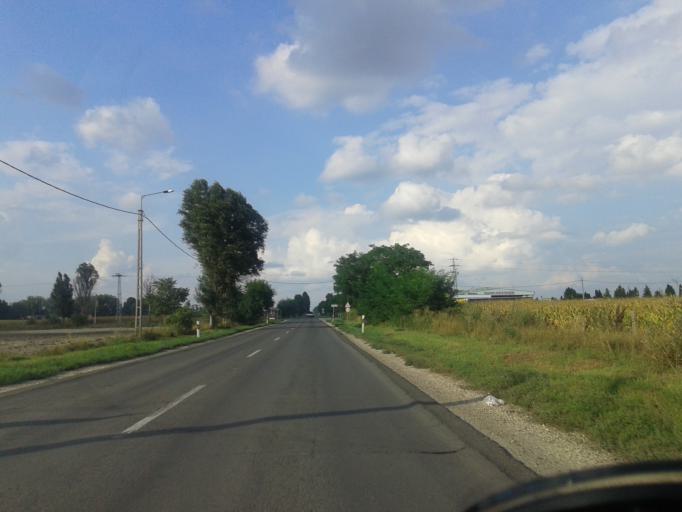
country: HU
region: Pest
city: Kiskunlachaza
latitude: 47.2045
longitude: 19.0125
